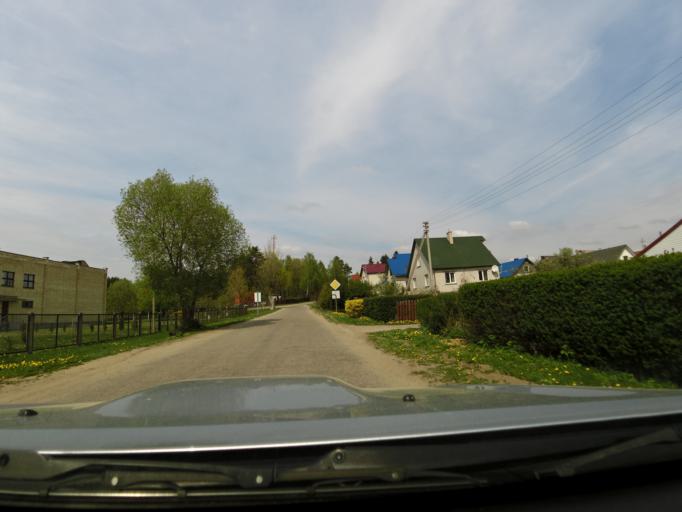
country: LT
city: Salcininkai
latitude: 54.4359
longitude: 25.3000
